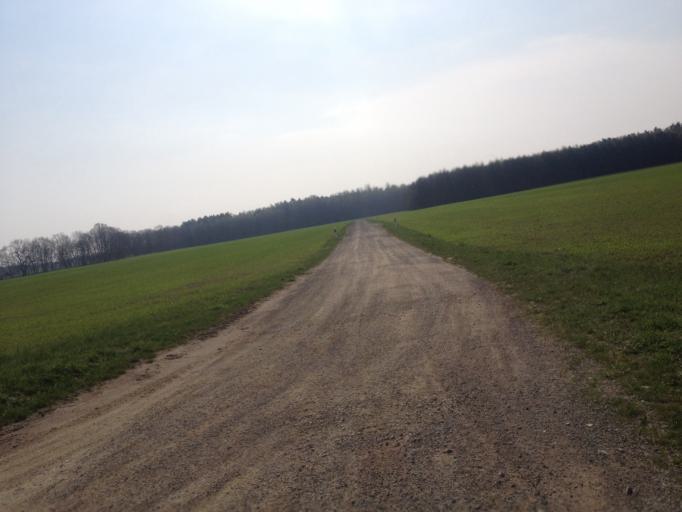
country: DE
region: Brandenburg
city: Drehnow
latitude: 51.8266
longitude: 14.3620
